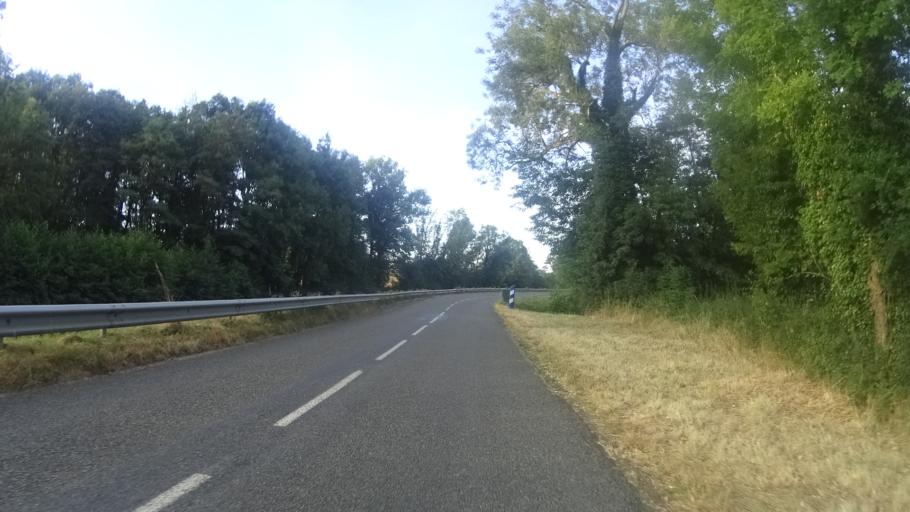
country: FR
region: Bourgogne
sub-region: Departement de Saone-et-Loire
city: Palinges
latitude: 46.4918
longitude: 4.1822
